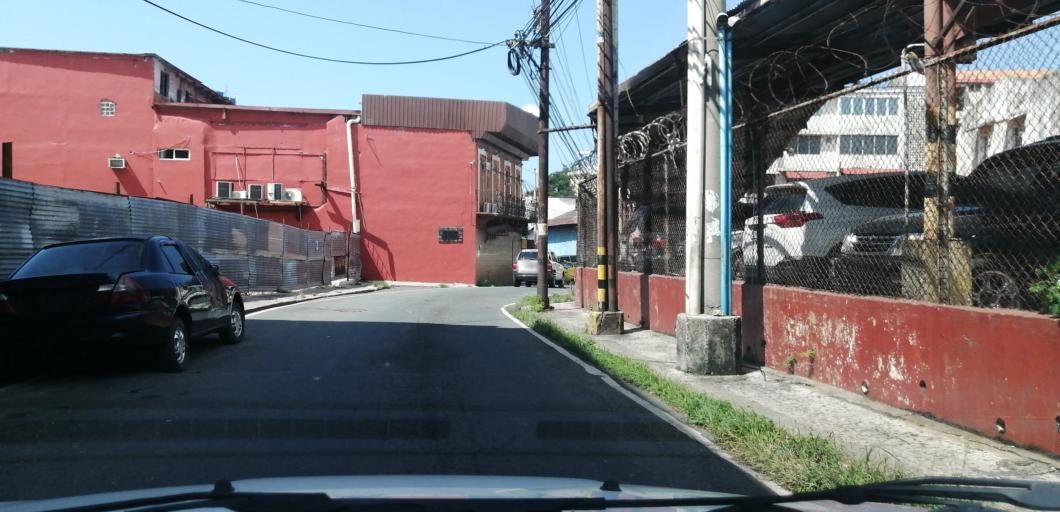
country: PA
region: Panama
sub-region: Distrito de Panama
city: Ancon
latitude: 8.9595
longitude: -79.5420
